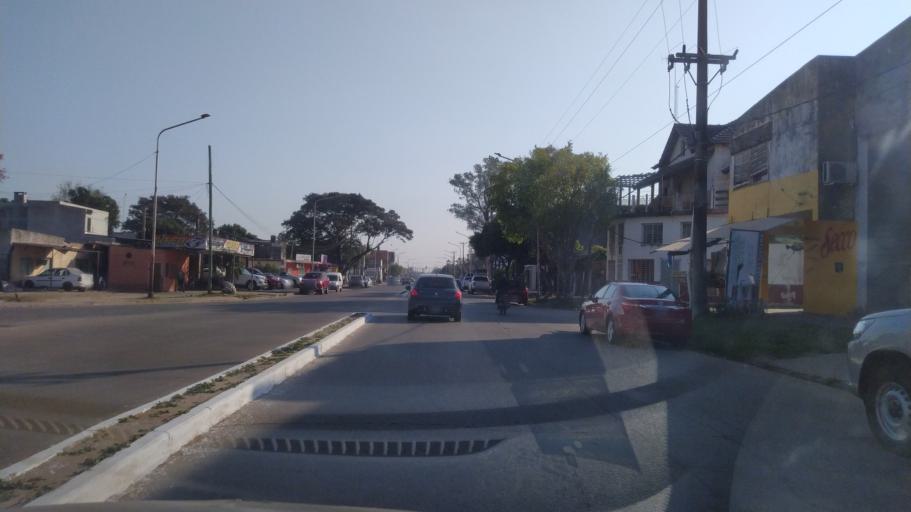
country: AR
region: Corrientes
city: Corrientes
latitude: -27.4892
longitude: -58.8167
